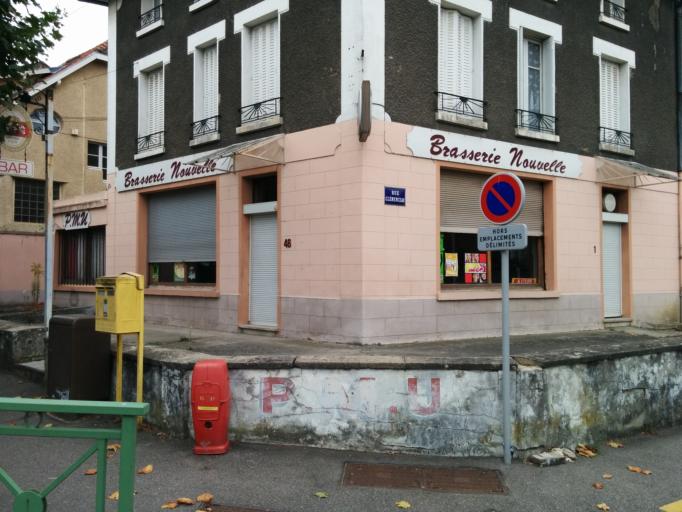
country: FR
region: Lorraine
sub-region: Departement de Meurthe-et-Moselle
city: Jarville-la-Malgrange
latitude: 48.6675
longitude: 6.1986
